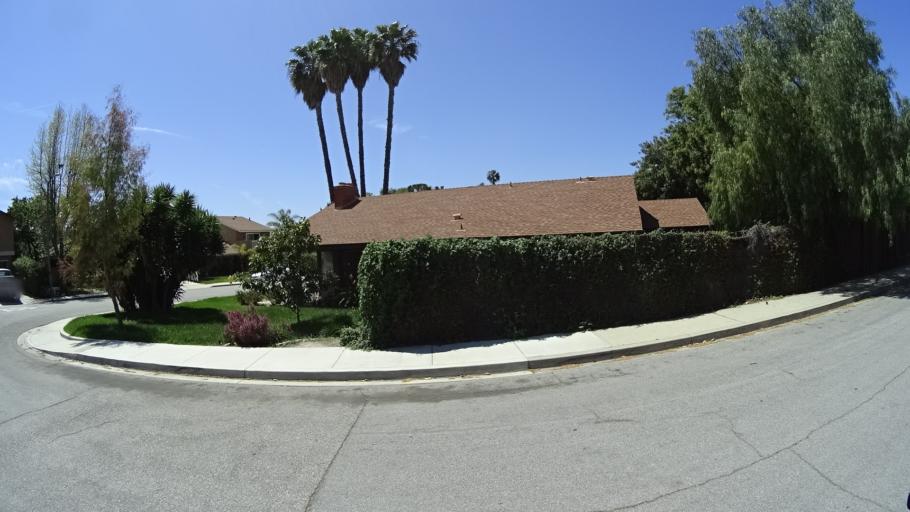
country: US
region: California
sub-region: Ventura County
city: Thousand Oaks
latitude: 34.2148
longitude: -118.8429
